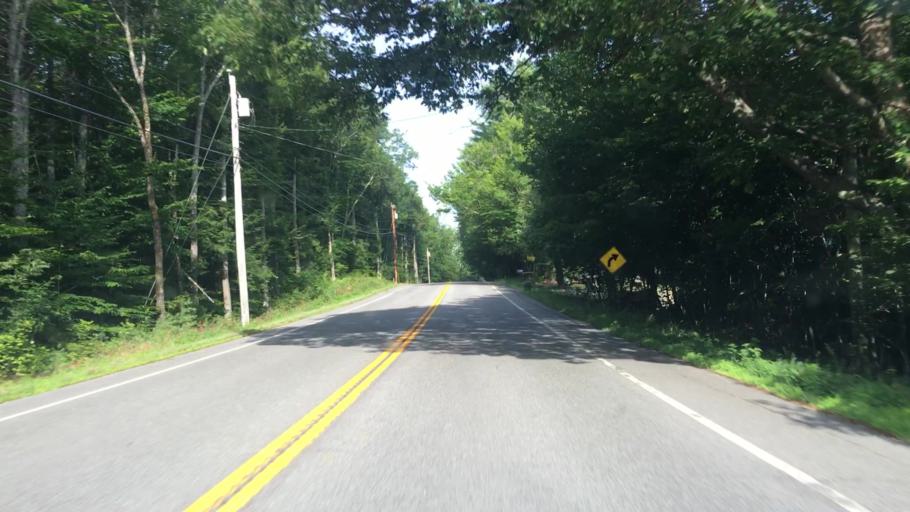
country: US
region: Maine
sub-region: York County
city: Limington
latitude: 43.7766
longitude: -70.7403
